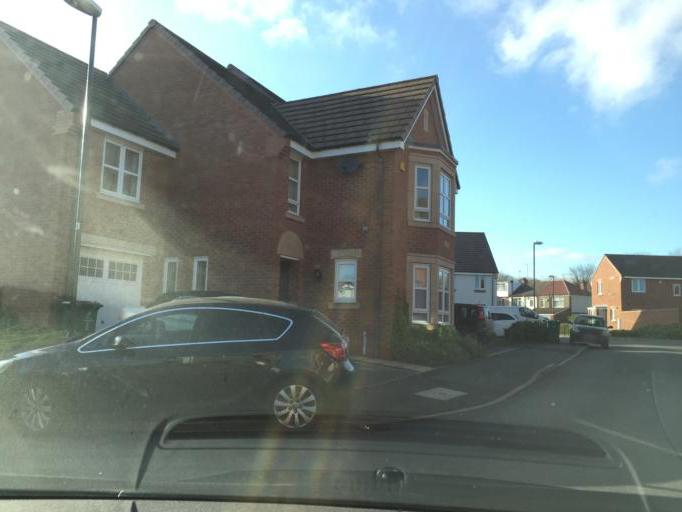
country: GB
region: England
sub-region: Coventry
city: Coventry
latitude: 52.3994
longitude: -1.4878
